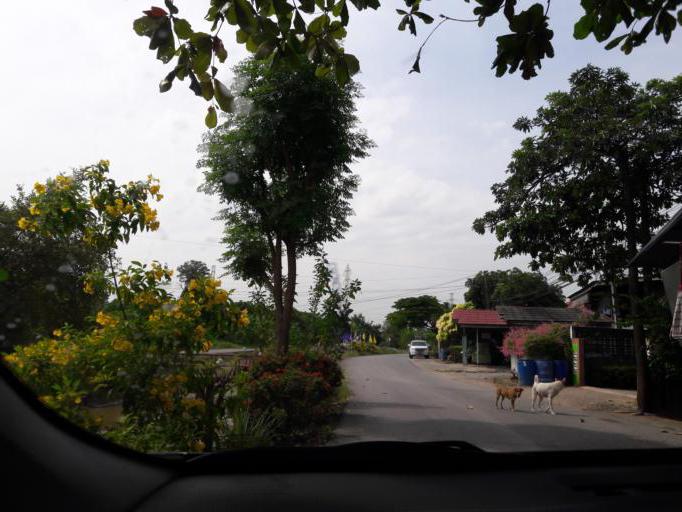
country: TH
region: Ang Thong
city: Ang Thong
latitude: 14.5828
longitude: 100.4768
